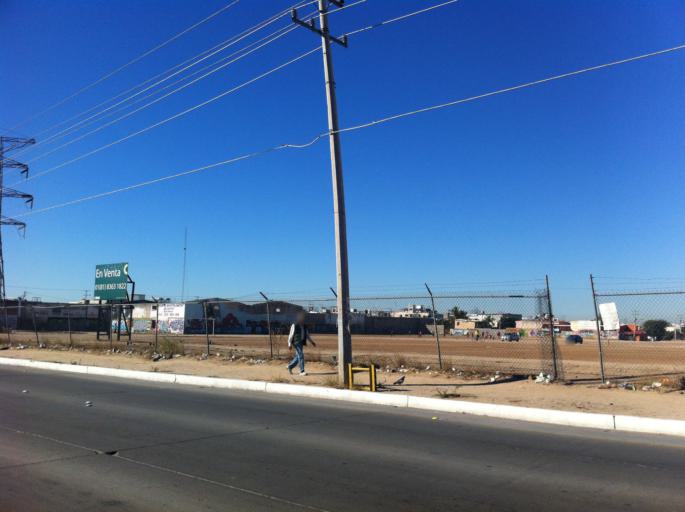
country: MX
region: Sonora
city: Hermosillo
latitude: 29.1166
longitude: -110.9926
